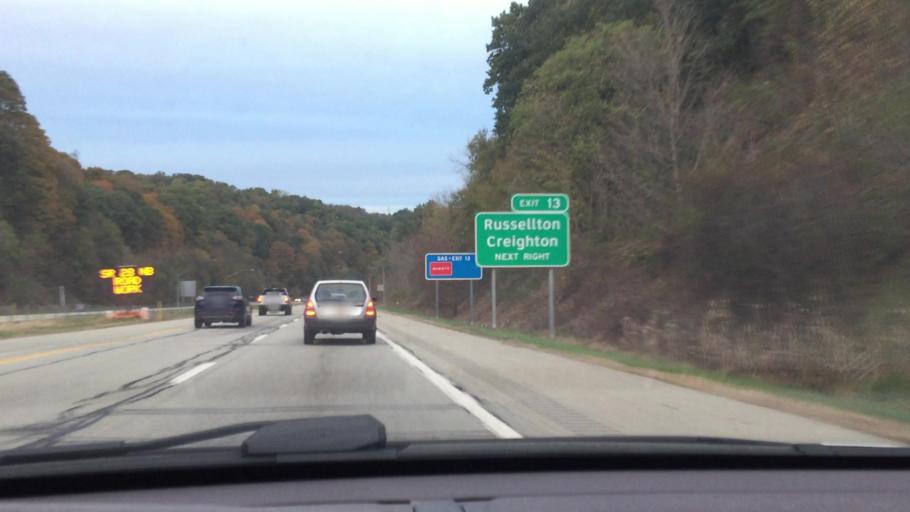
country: US
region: Pennsylvania
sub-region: Westmoreland County
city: Arnold
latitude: 40.5754
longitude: -79.7867
